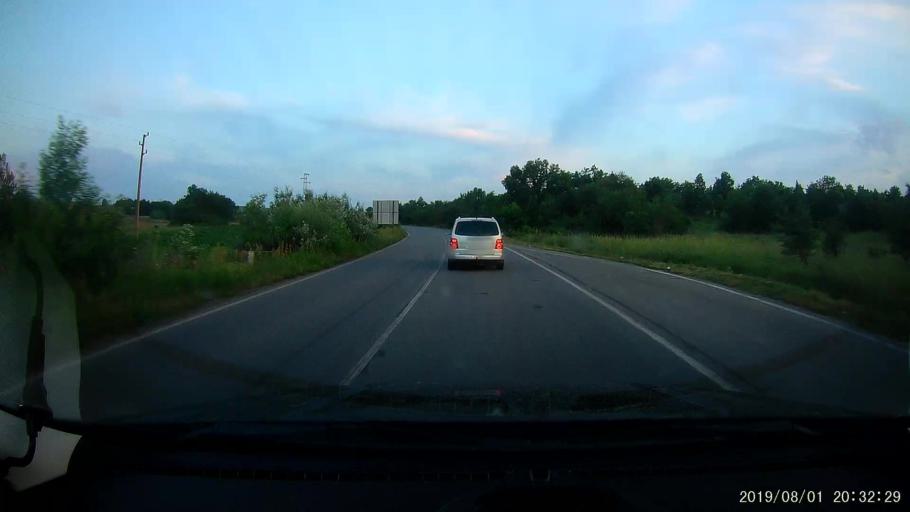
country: BG
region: Yambol
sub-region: Obshtina Elkhovo
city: Elkhovo
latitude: 42.1215
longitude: 26.5298
